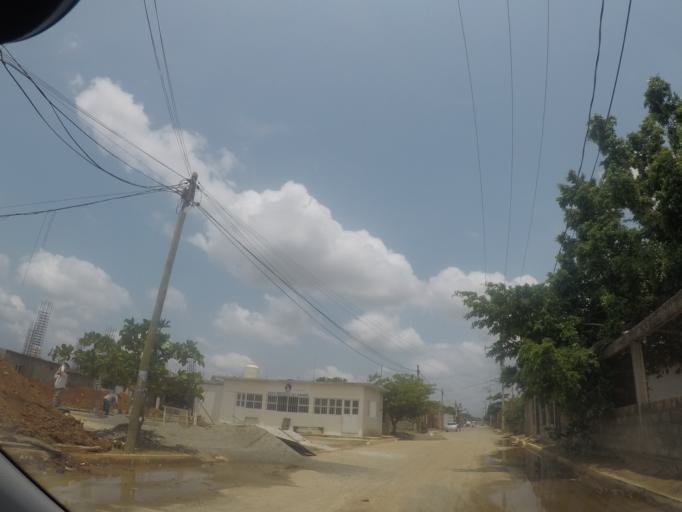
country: MX
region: Oaxaca
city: El Espinal
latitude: 16.5564
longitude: -94.9456
